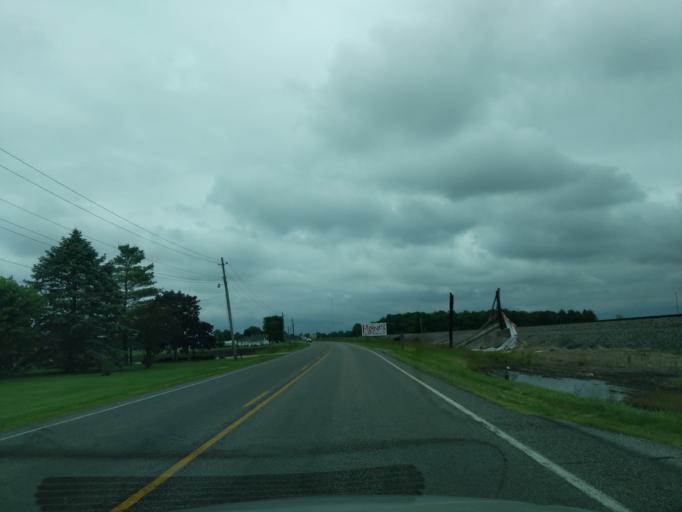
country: US
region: Indiana
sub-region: Madison County
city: Elwood
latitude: 40.2769
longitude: -85.8783
